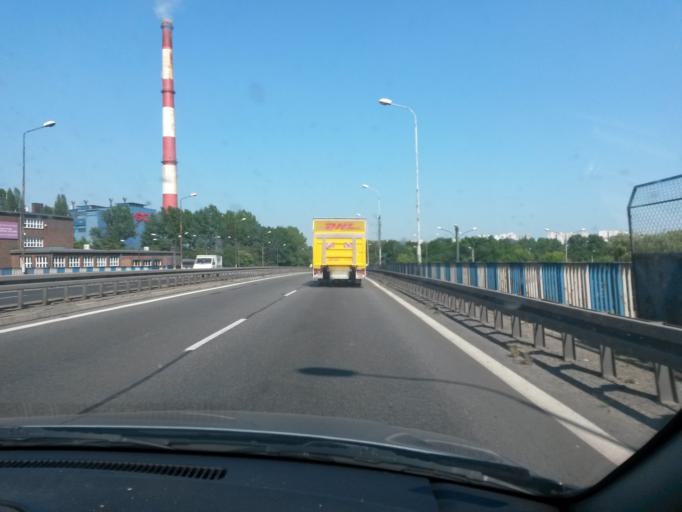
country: PL
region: Silesian Voivodeship
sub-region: Powiat bedzinski
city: Bedzin
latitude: 50.3006
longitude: 19.1350
